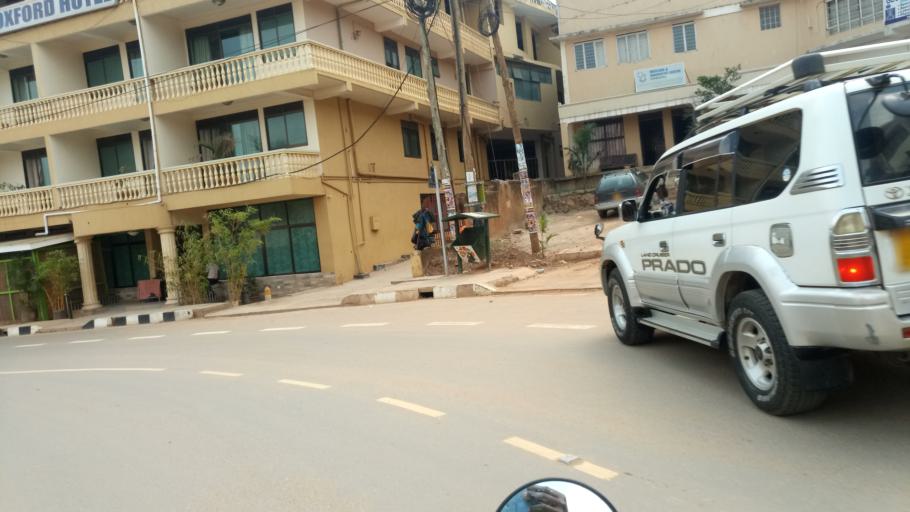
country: UG
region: Western Region
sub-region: Mbarara District
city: Mbarara
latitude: -0.6084
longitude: 30.6621
